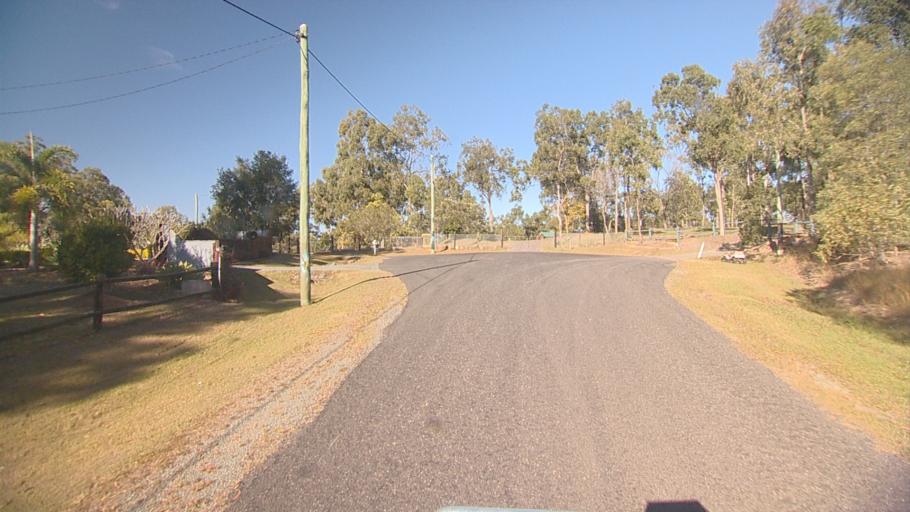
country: AU
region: Queensland
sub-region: Ipswich
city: Springfield Lakes
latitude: -27.7039
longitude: 152.9314
